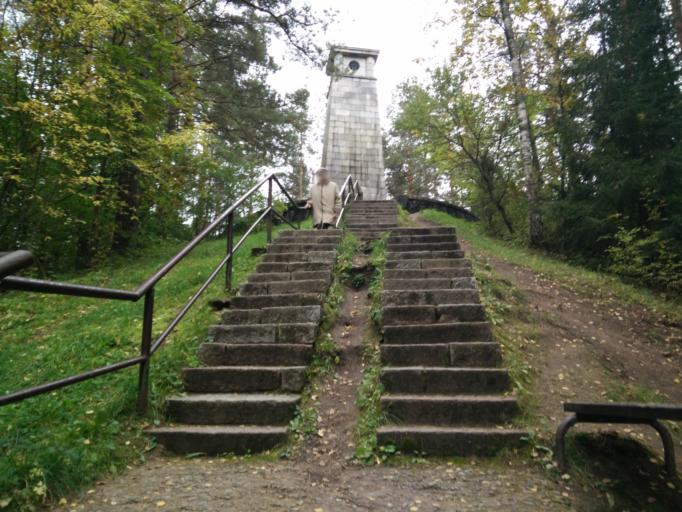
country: LT
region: Utenos apskritis
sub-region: Anyksciai
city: Anyksciai
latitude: 55.5122
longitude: 25.1226
